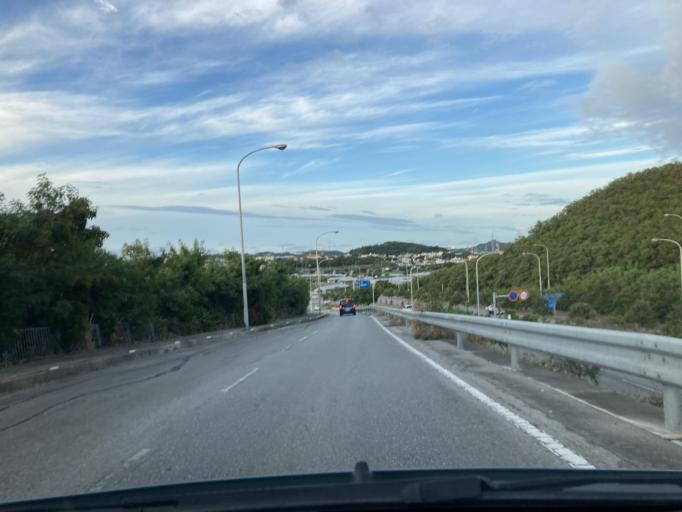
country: JP
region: Okinawa
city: Tomigusuku
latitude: 26.1739
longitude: 127.7270
